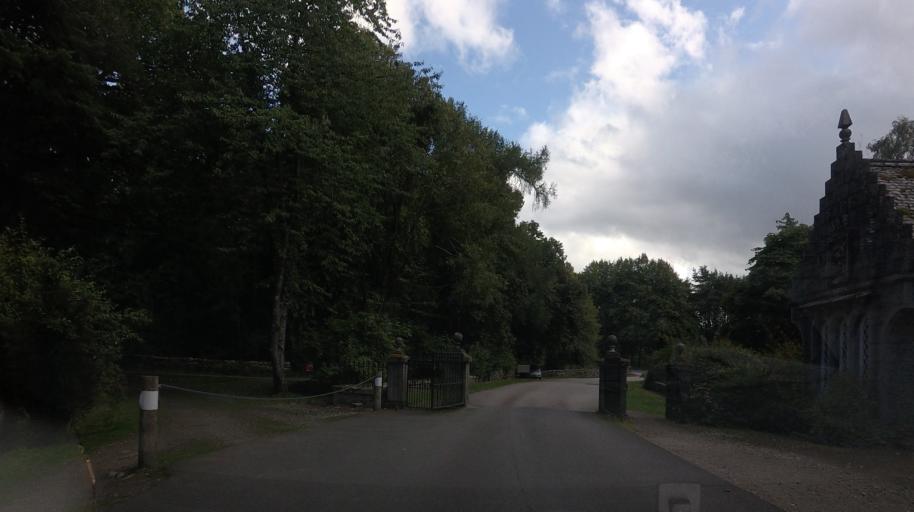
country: GB
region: Scotland
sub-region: Aberdeenshire
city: Banchory
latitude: 57.0574
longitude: -2.4269
